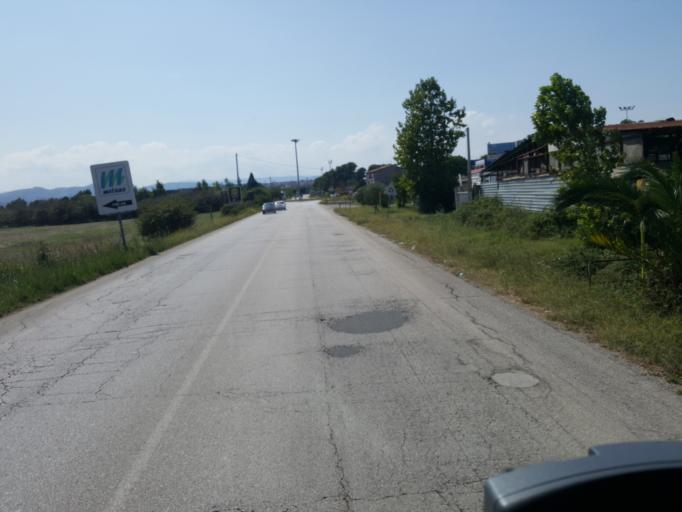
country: IT
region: Abruzzo
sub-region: Provincia di Chieti
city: Salvo Marina
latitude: 42.0580
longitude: 14.7592
